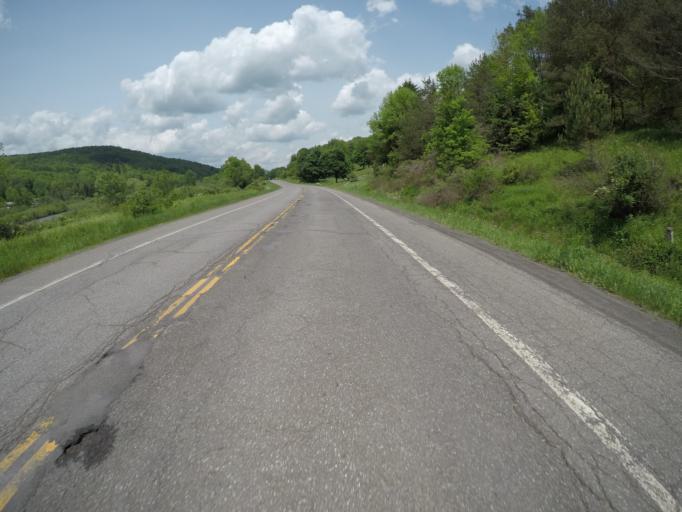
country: US
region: New York
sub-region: Delaware County
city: Stamford
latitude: 42.1851
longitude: -74.5984
